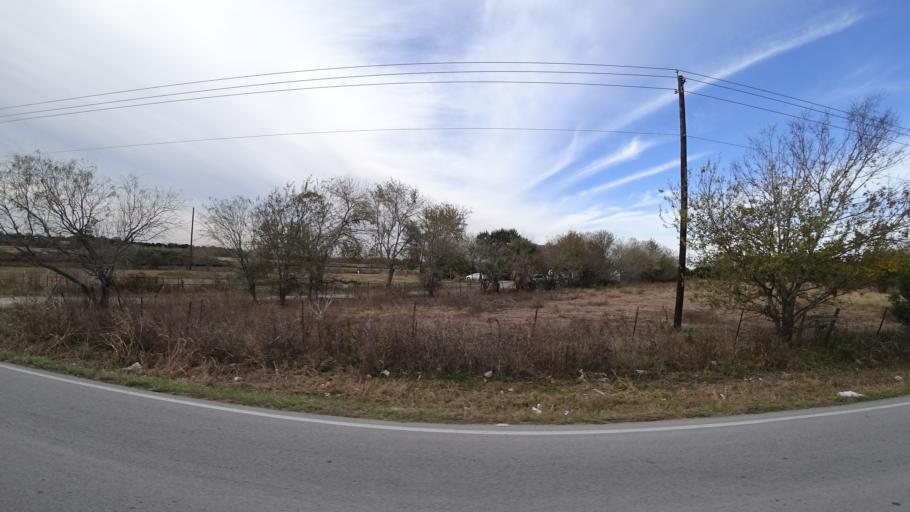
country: US
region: Texas
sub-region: Travis County
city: Onion Creek
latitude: 30.1463
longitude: -97.7303
